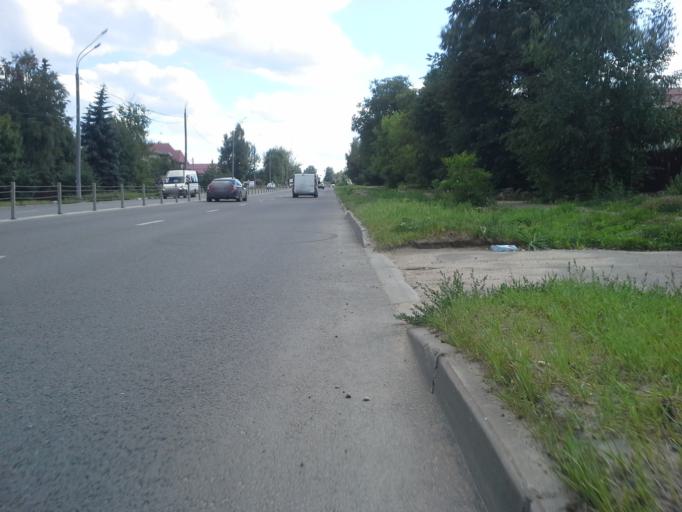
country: RU
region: Moskovskaya
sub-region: Podol'skiy Rayon
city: Podol'sk
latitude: 55.3986
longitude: 37.5501
